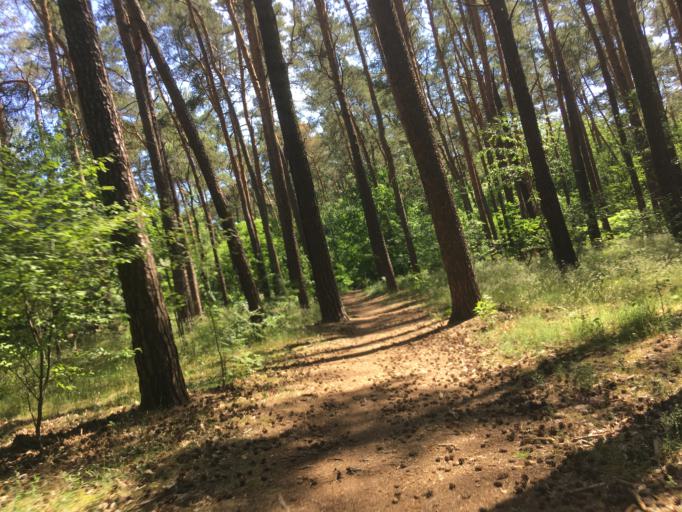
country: DE
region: Berlin
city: Schmockwitz
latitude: 52.3854
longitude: 13.6395
